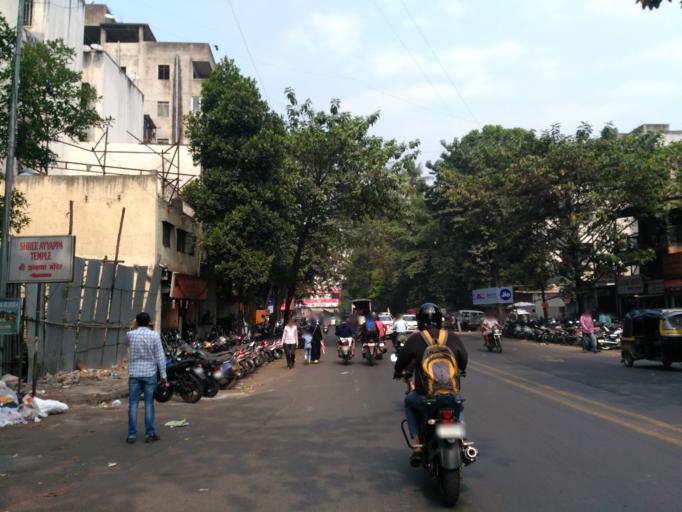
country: IN
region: Maharashtra
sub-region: Pune Division
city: Pune
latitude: 18.5182
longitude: 73.8684
